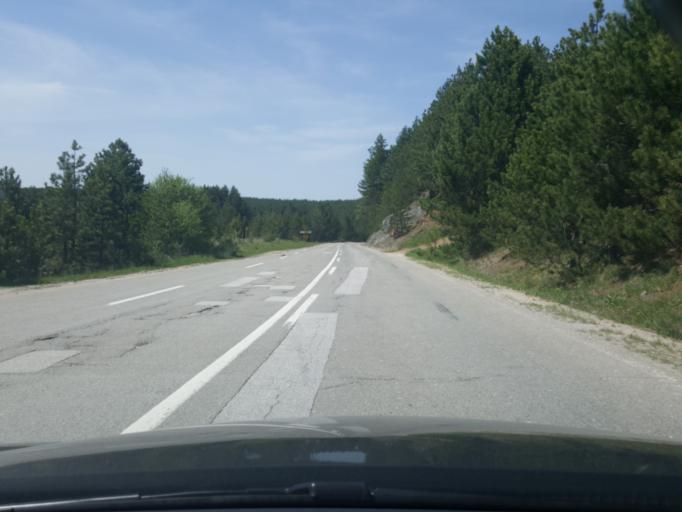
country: RS
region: Central Serbia
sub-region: Zlatiborski Okrug
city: Cajetina
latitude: 43.8282
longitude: 19.6406
